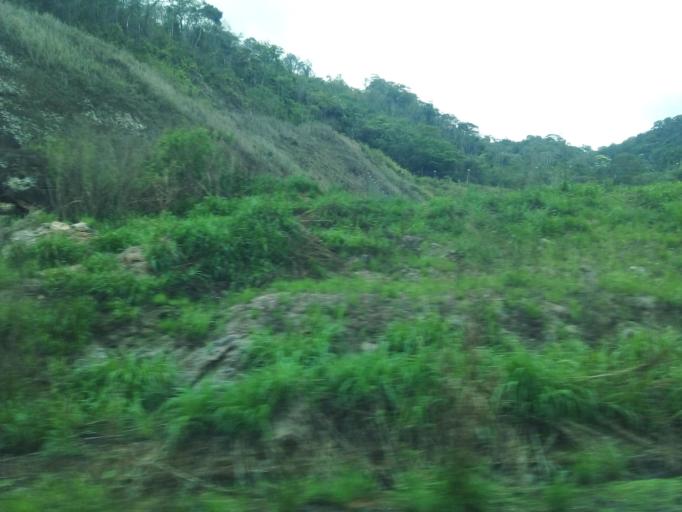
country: BR
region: Minas Gerais
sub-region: Joao Monlevade
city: Joao Monlevade
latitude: -19.8553
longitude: -43.1205
